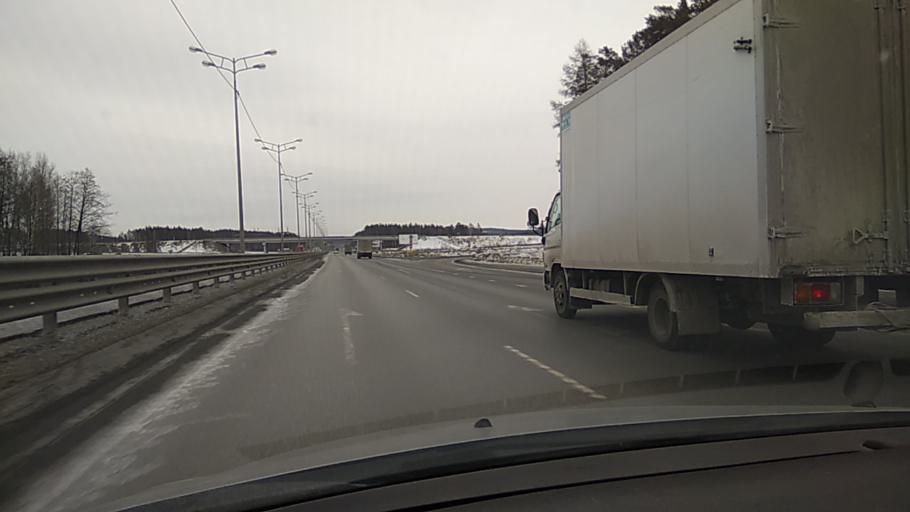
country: RU
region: Sverdlovsk
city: Severka
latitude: 56.8332
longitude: 60.3142
